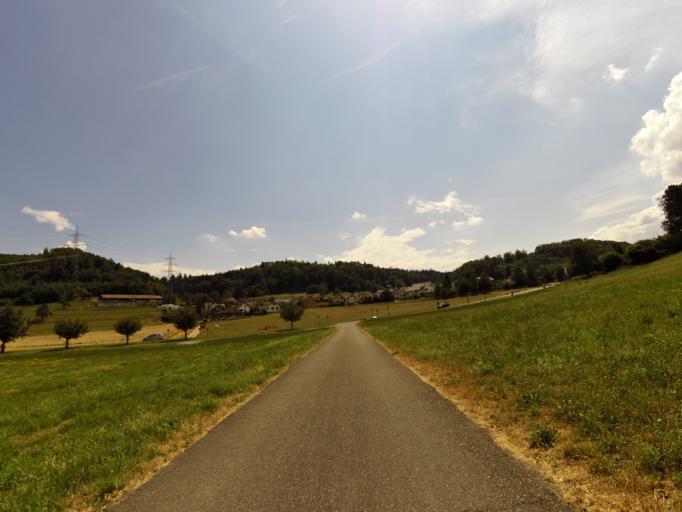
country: CH
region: Aargau
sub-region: Bezirk Bremgarten
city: Hagglingen
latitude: 47.4131
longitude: 8.2432
